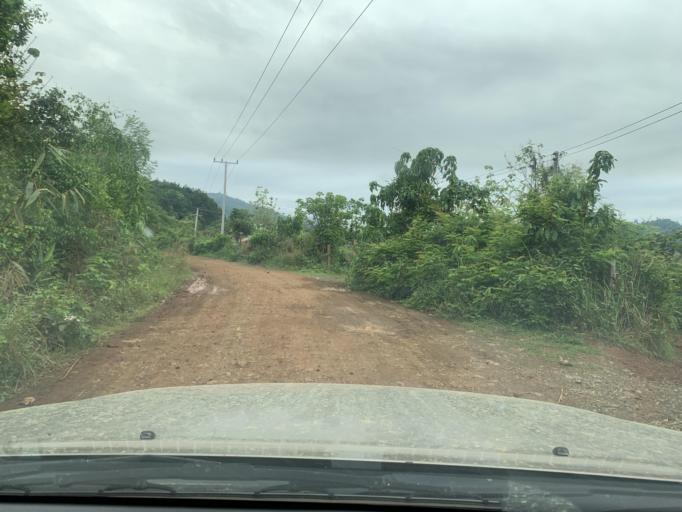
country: TH
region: Nan
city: Mae Charim
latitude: 18.4125
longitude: 101.4413
